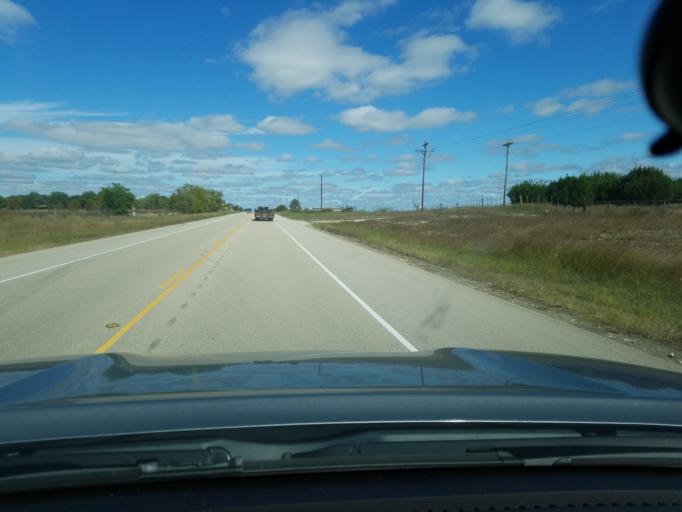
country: US
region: Texas
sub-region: Hamilton County
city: Hamilton
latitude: 31.6624
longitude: -98.1413
